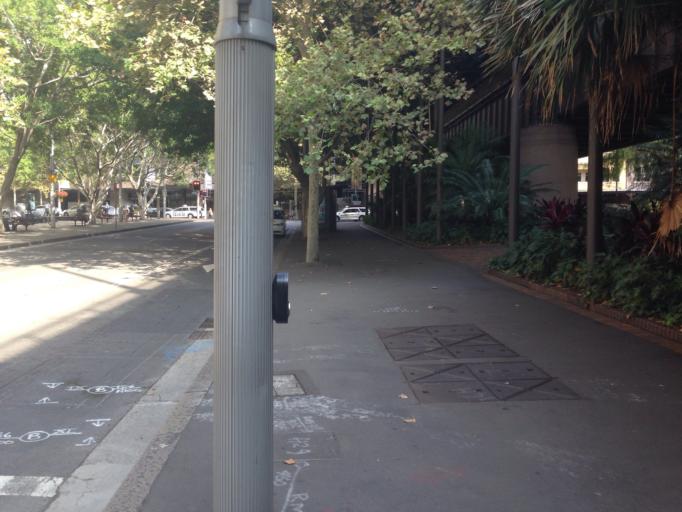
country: AU
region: New South Wales
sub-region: City of Sydney
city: Sydney
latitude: -33.8615
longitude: 151.2092
